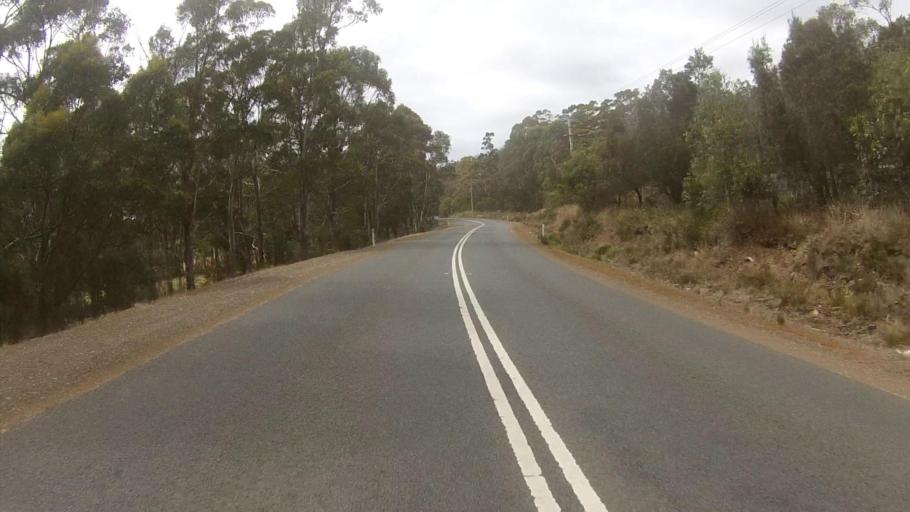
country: AU
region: Tasmania
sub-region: Kingborough
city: Margate
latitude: -43.0021
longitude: 147.2340
